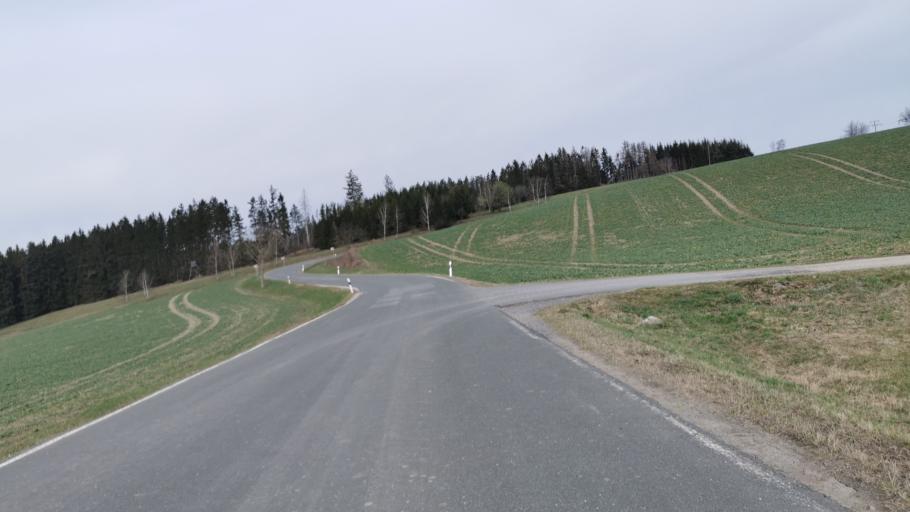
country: DE
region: Thuringia
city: Leutenberg
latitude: 50.5245
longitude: 11.4458
